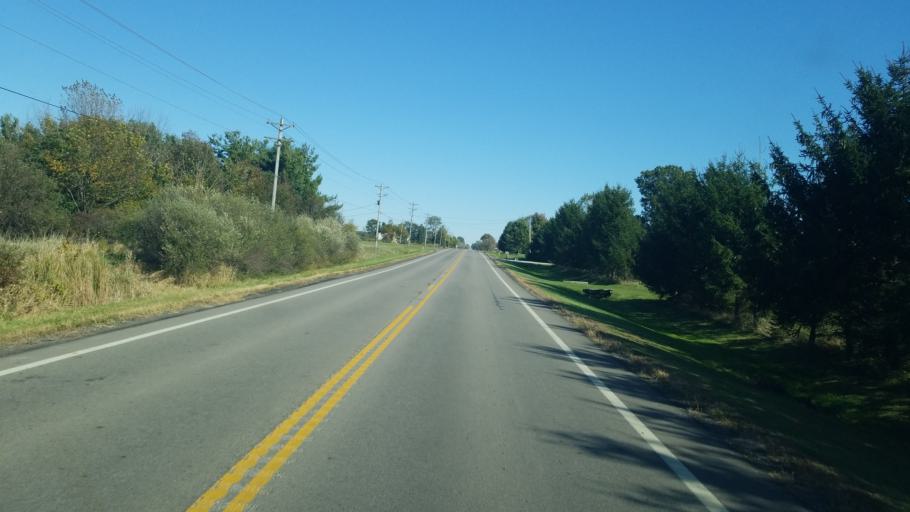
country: US
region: Ohio
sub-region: Lorain County
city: Wellington
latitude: 41.0284
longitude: -82.2591
